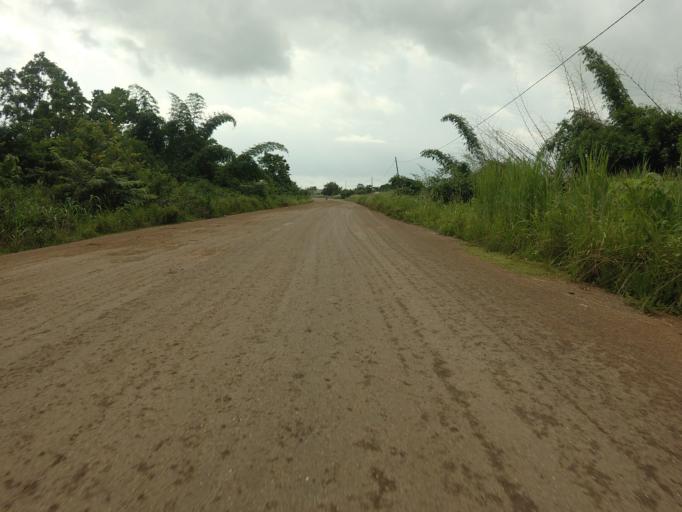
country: GH
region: Volta
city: Kpandu
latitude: 6.9466
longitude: 0.4603
